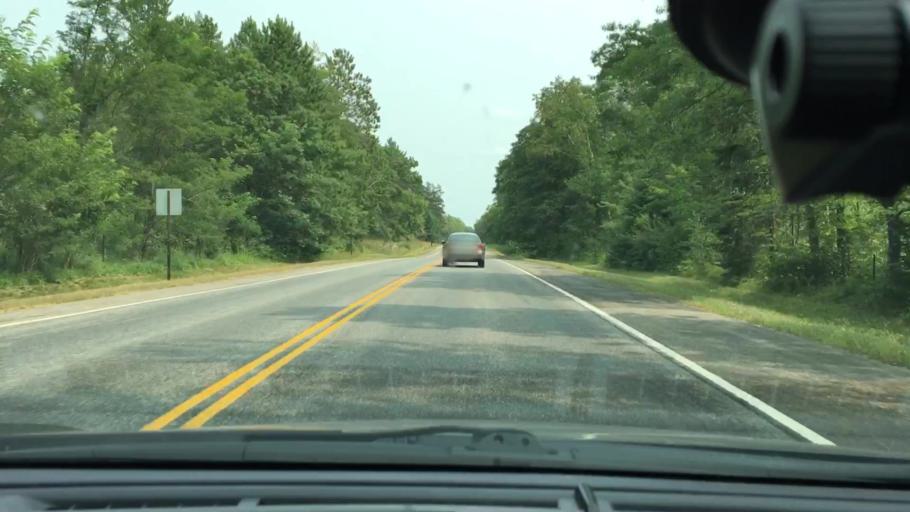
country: US
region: Minnesota
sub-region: Cass County
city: East Gull Lake
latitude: 46.4128
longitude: -94.3268
